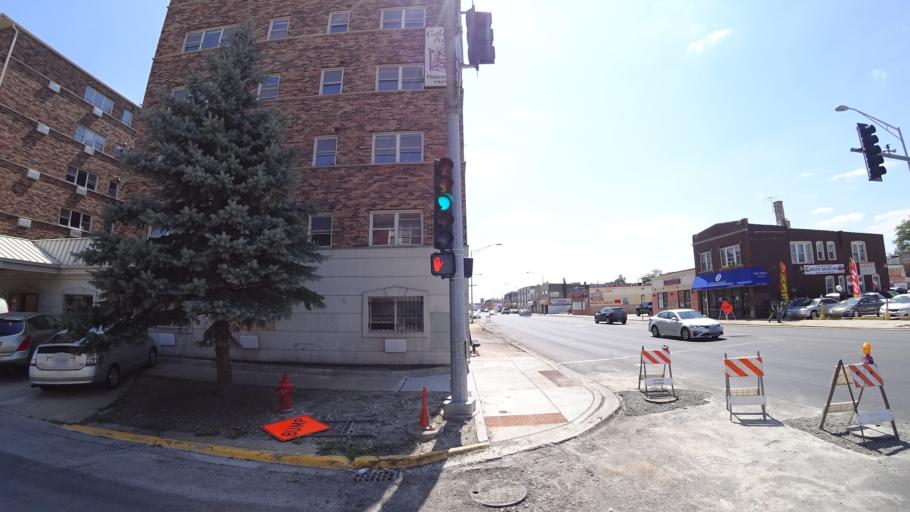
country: US
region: Illinois
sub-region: Cook County
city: Cicero
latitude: 41.8549
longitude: -87.7442
